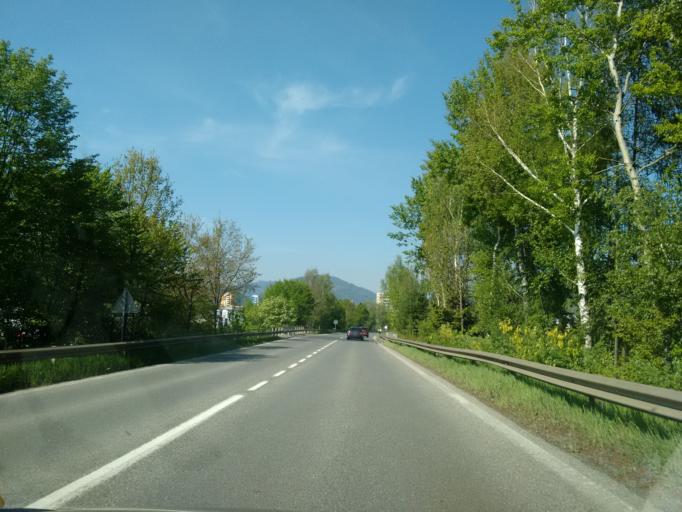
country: AT
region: Styria
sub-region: Politischer Bezirk Bruck-Muerzzuschlag
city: Kapfenberg
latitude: 47.4512
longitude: 15.3205
